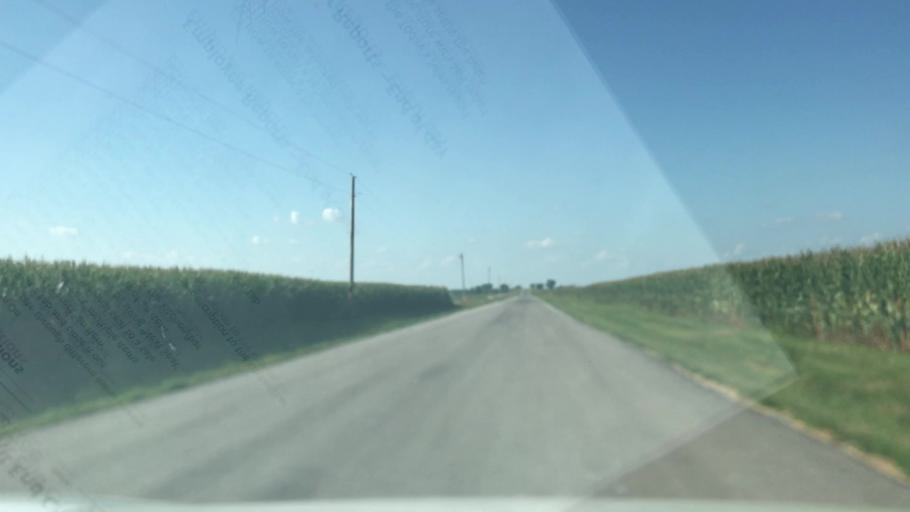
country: US
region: Illinois
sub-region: Washington County
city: Okawville
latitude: 38.4187
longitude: -89.4776
